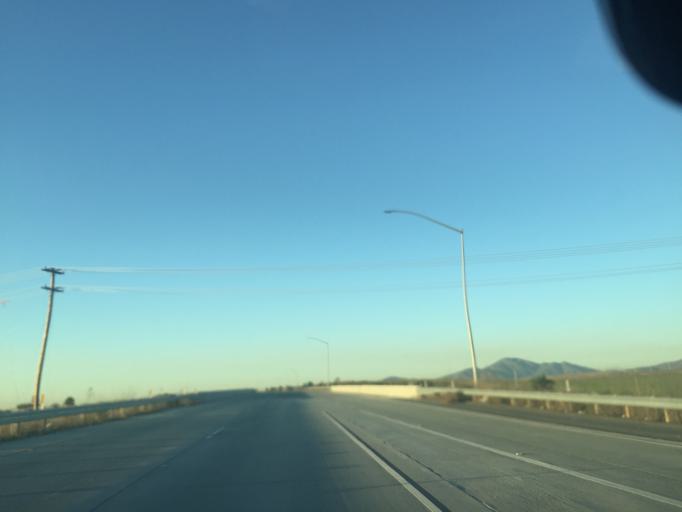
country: MX
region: Baja California
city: Tijuana
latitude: 32.5667
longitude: -116.9482
